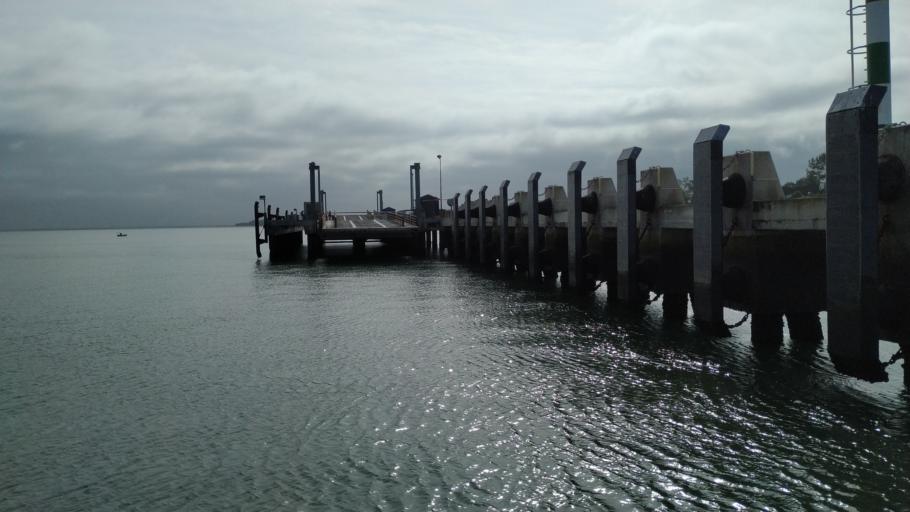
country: PT
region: Setubal
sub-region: Setubal
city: Setubal
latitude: 38.4679
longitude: -8.8637
